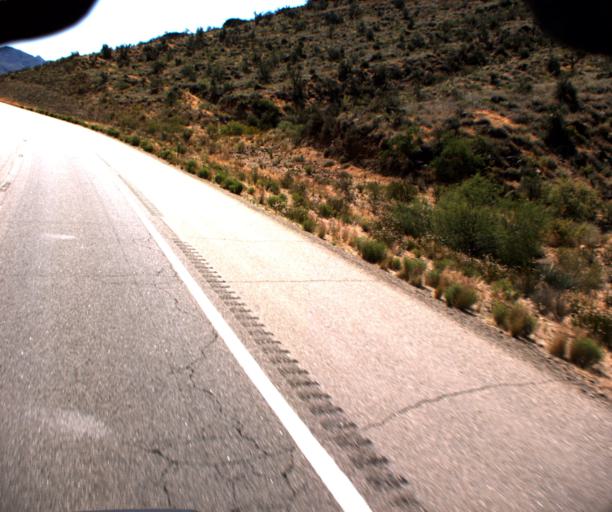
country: US
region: Arizona
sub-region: Yavapai County
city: Bagdad
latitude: 34.4478
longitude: -113.2819
